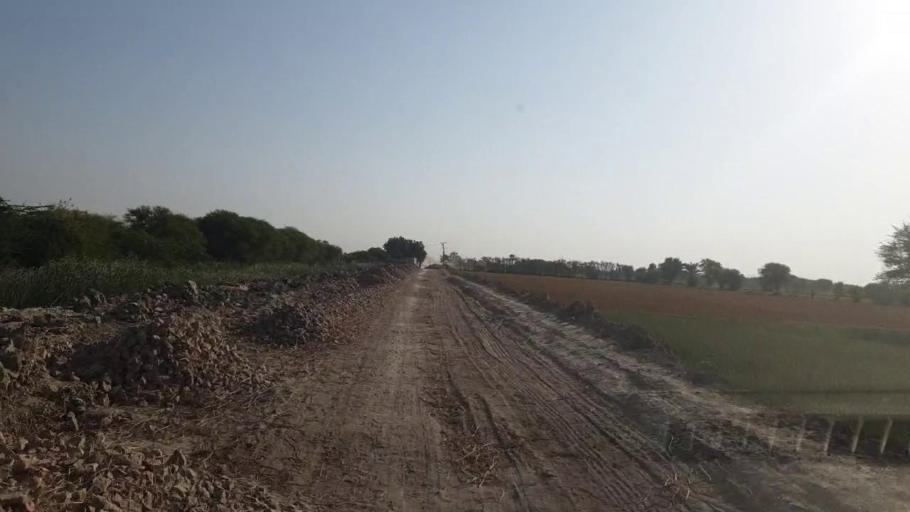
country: PK
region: Sindh
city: Talhar
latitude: 24.9265
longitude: 68.7479
